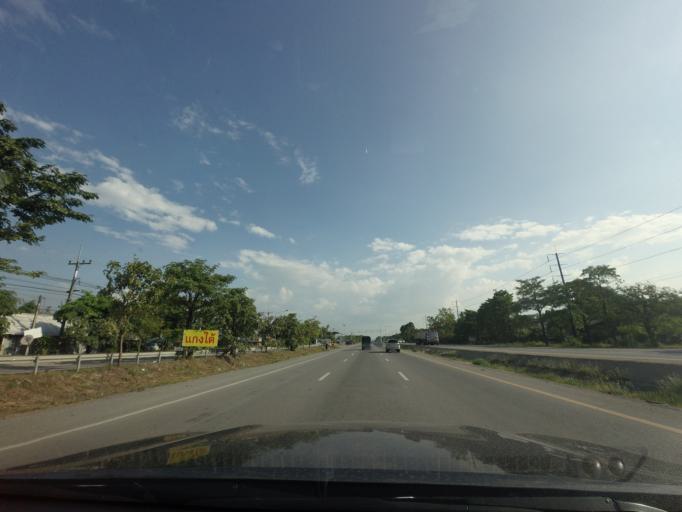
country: TH
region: Sara Buri
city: Chaloem Phra Kiat
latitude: 14.6477
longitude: 100.8852
